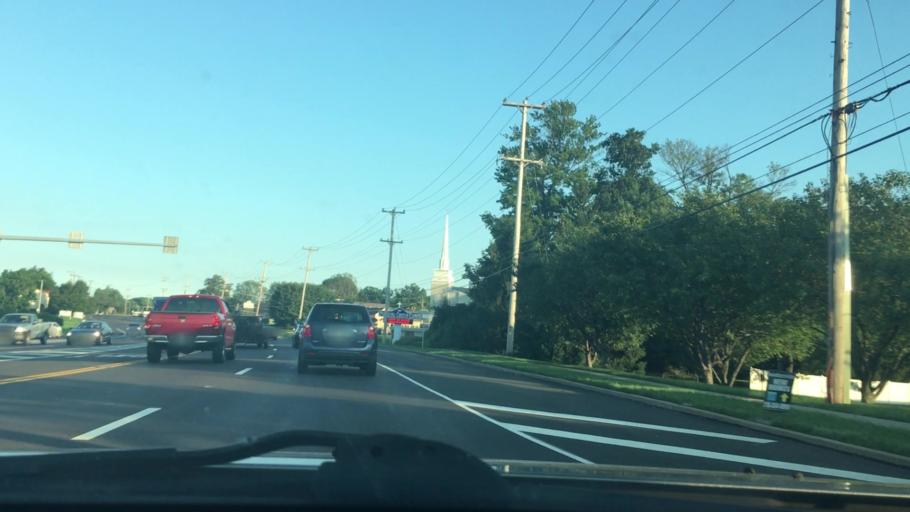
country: US
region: Pennsylvania
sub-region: Bucks County
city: Eddington
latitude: 40.1151
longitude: -74.9579
